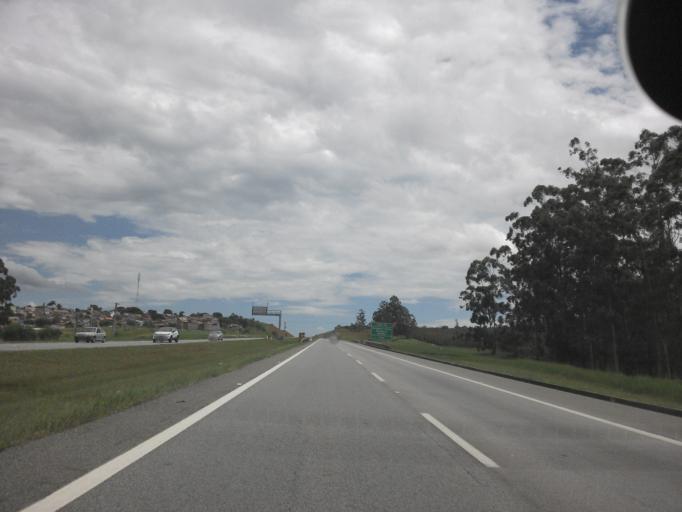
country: BR
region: Sao Paulo
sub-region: Cacapava
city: Cacapava
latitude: -23.1091
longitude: -45.6429
